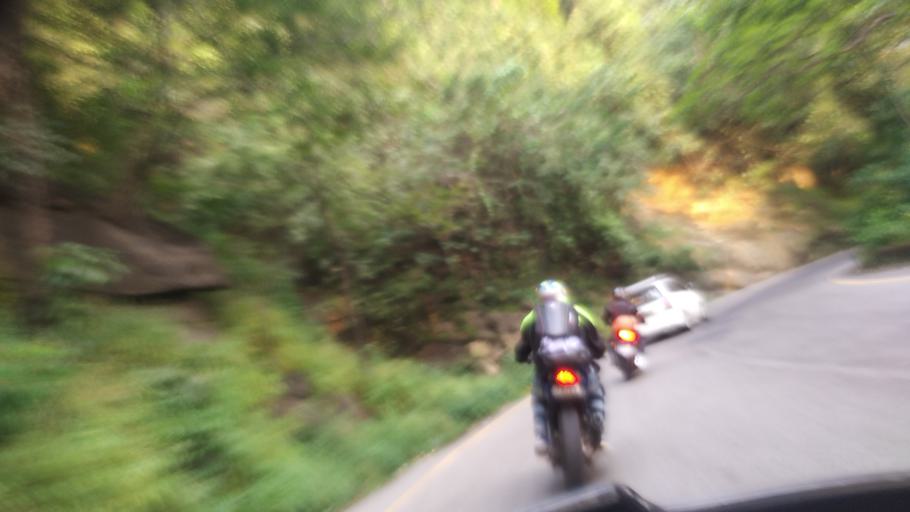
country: IN
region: Kerala
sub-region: Wayanad
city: Kalpetta
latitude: 11.5102
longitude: 76.0243
